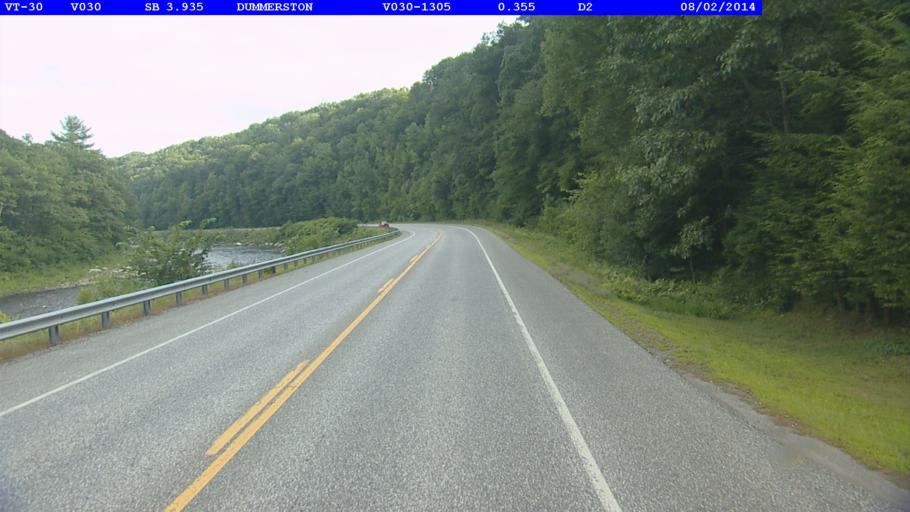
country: US
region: Vermont
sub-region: Windham County
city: West Brattleboro
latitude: 42.9019
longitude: -72.6013
